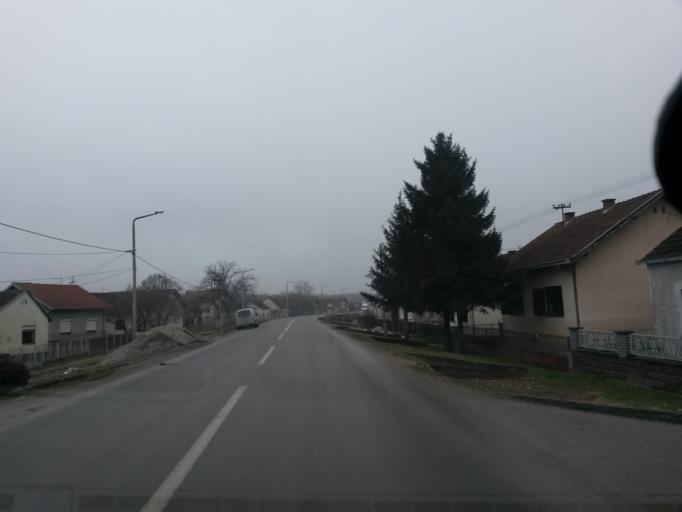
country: BA
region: Brcko
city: Brcko
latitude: 44.8919
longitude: 18.8253
